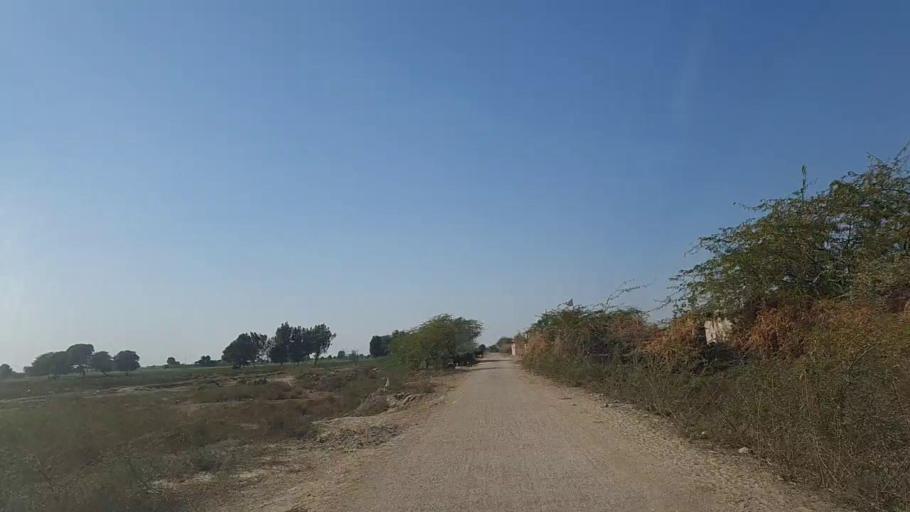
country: PK
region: Sindh
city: Naukot
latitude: 25.0147
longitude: 69.3603
